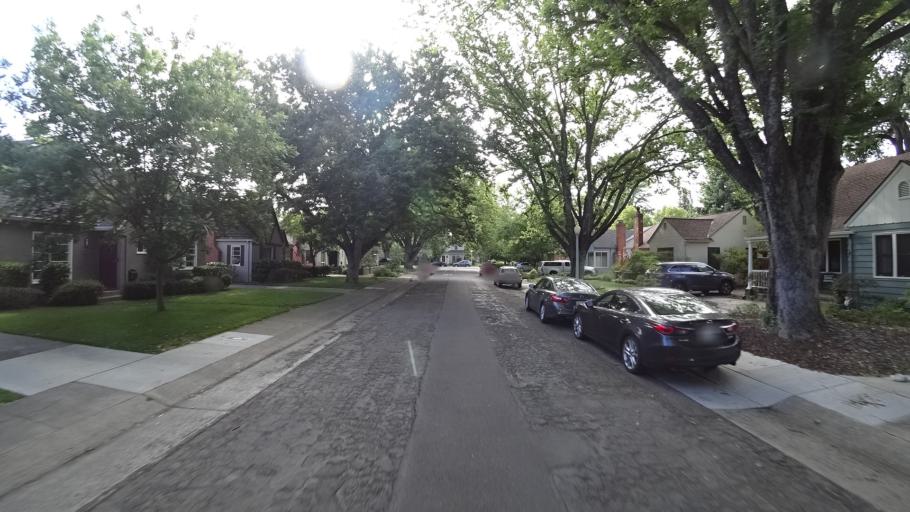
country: US
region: California
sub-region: Sacramento County
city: Sacramento
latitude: 38.5537
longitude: -121.5050
